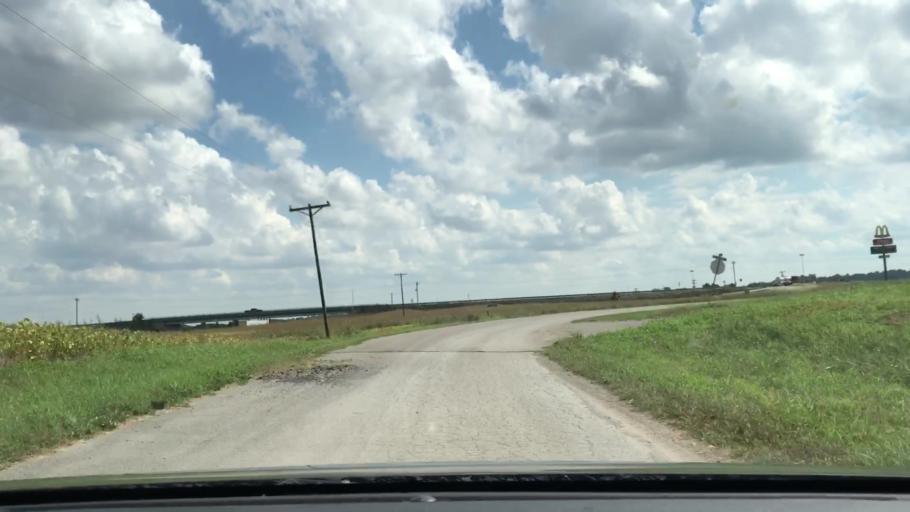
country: US
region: Kentucky
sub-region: Christian County
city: Oak Grove
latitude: 36.6822
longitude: -87.4080
